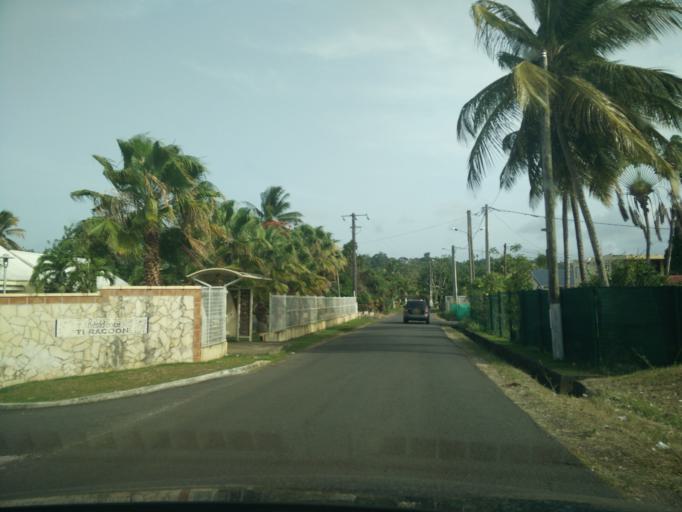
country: GP
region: Guadeloupe
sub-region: Guadeloupe
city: Petit-Bourg
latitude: 16.1295
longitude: -61.5883
